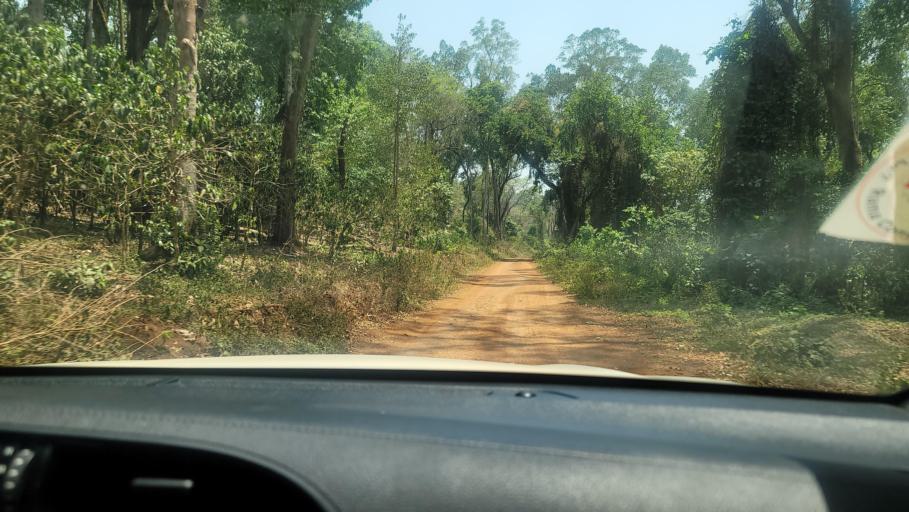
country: ET
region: Southern Nations, Nationalities, and People's Region
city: Bonga
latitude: 7.5083
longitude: 36.2270
